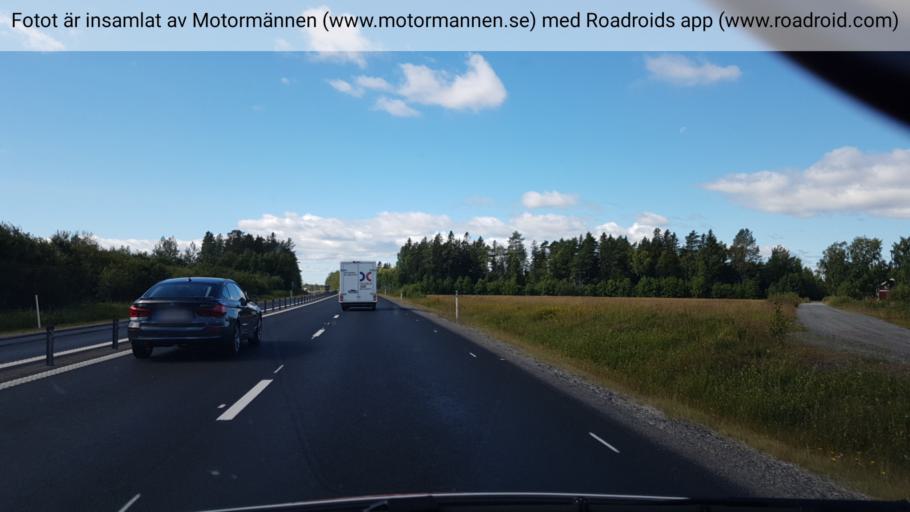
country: SE
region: Vaesterbotten
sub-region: Umea Kommun
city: Hoernefors
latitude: 63.6375
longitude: 19.9058
